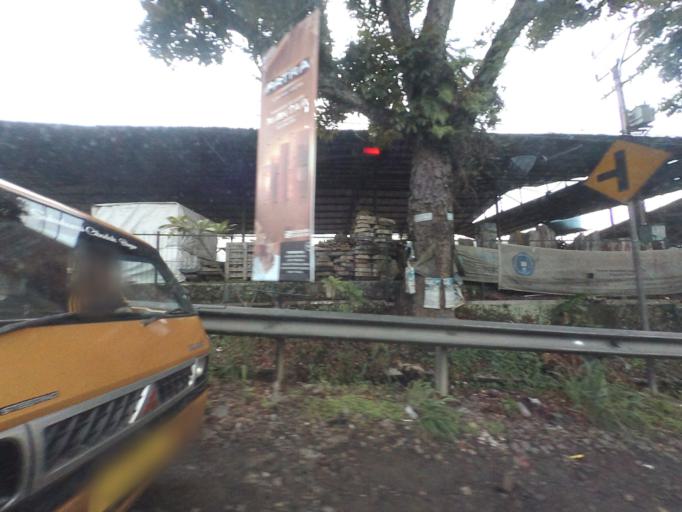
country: ID
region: West Java
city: Cicurug
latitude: -6.8414
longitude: 106.7616
